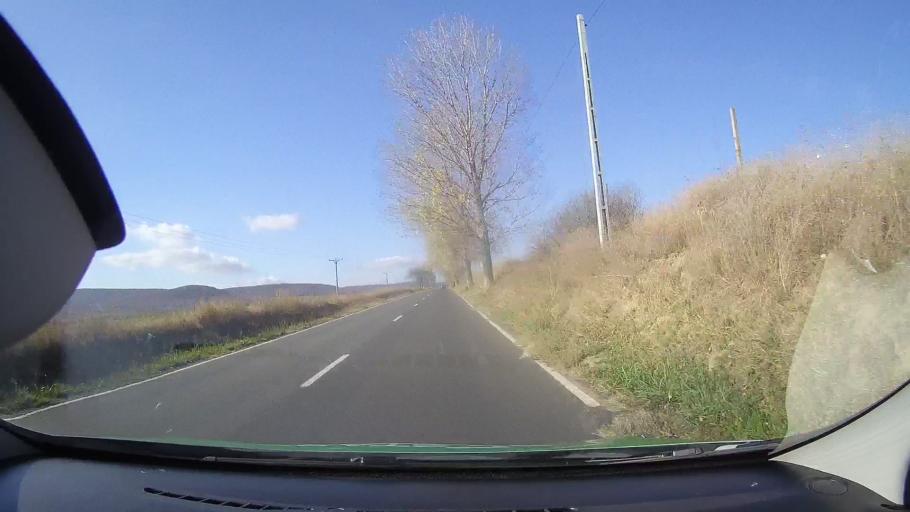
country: RO
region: Tulcea
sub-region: Comuna Sarichioi
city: Enisala
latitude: 44.8792
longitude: 28.7866
